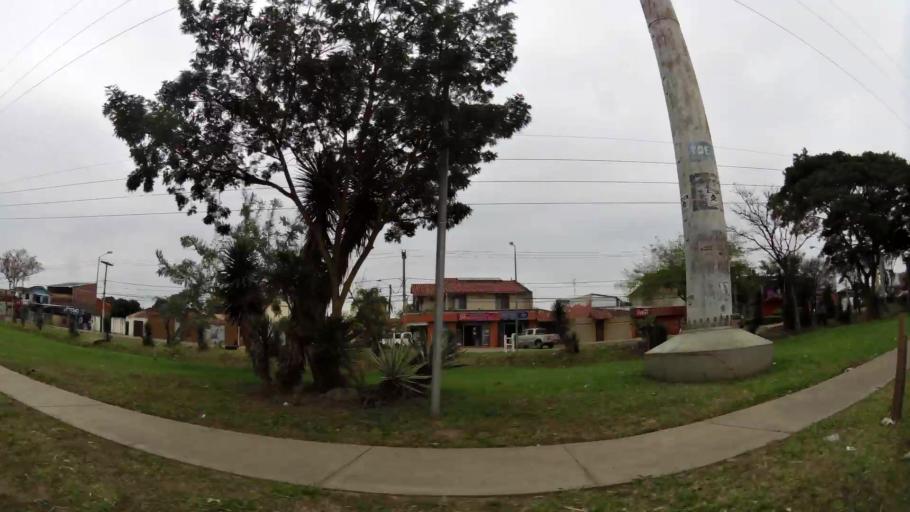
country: BO
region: Santa Cruz
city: Santa Cruz de la Sierra
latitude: -17.7690
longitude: -63.1471
